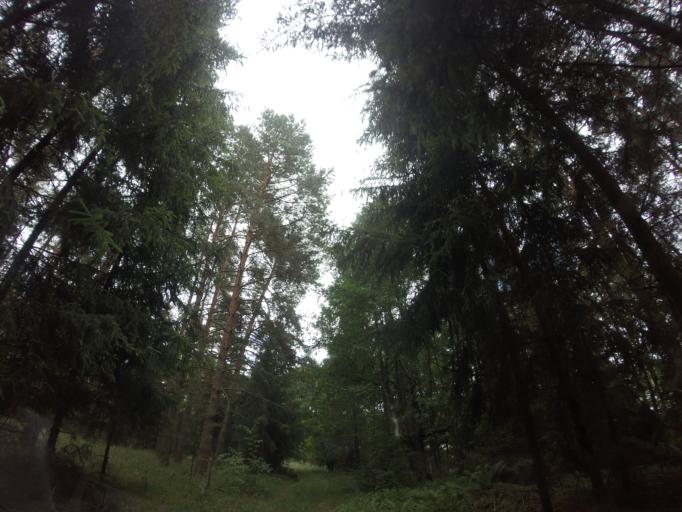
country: PL
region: West Pomeranian Voivodeship
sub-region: Powiat choszczenski
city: Krzecin
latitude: 53.0211
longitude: 15.5436
